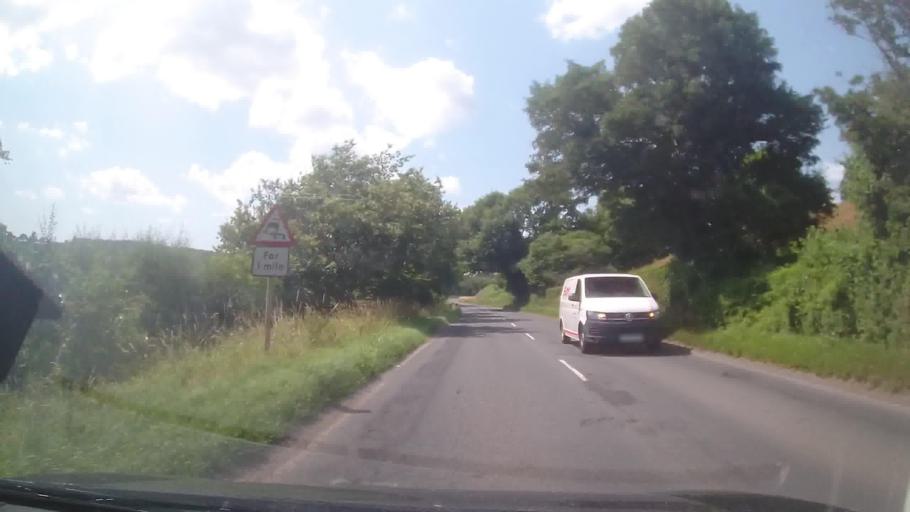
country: GB
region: England
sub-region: Herefordshire
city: Bodenham
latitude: 52.1697
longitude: -2.6906
